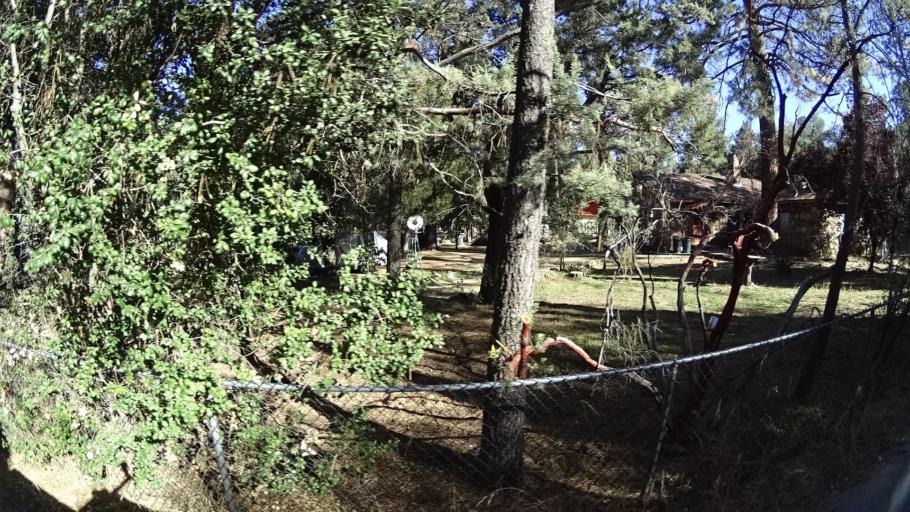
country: US
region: California
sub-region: San Diego County
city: Pine Valley
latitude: 32.8248
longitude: -116.5258
